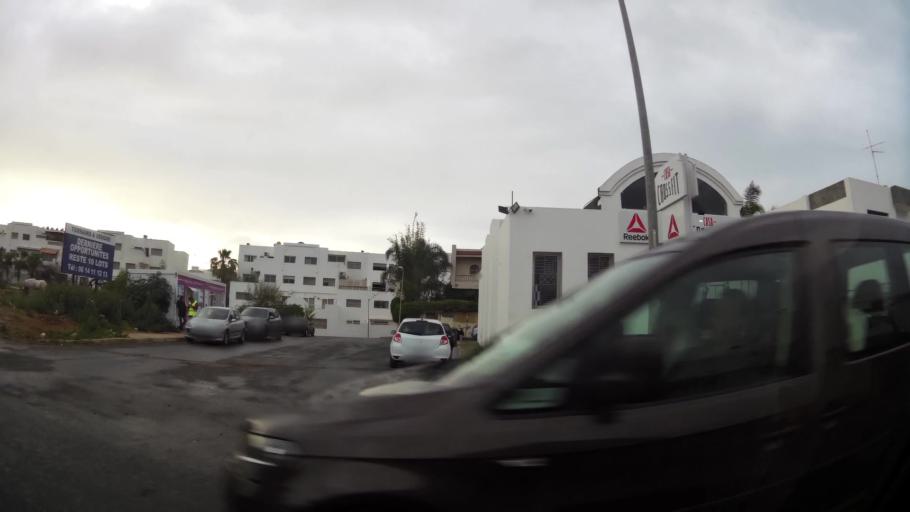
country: MA
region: Grand Casablanca
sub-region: Casablanca
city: Casablanca
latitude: 33.5795
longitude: -7.6801
